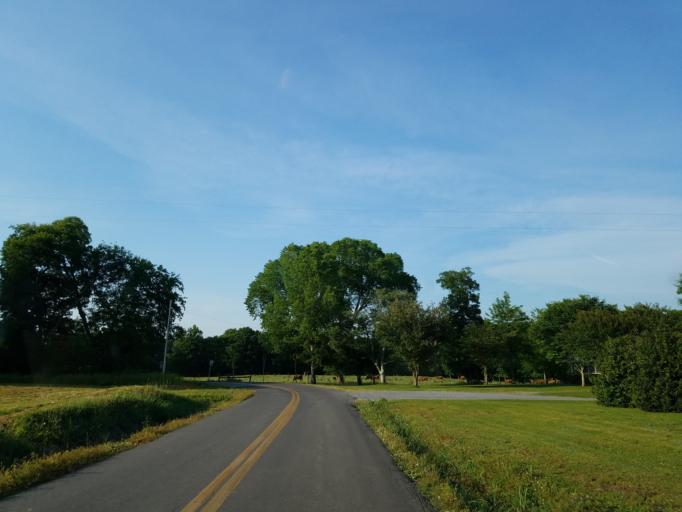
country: US
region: Georgia
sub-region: Gordon County
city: Calhoun
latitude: 34.5209
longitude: -85.1189
